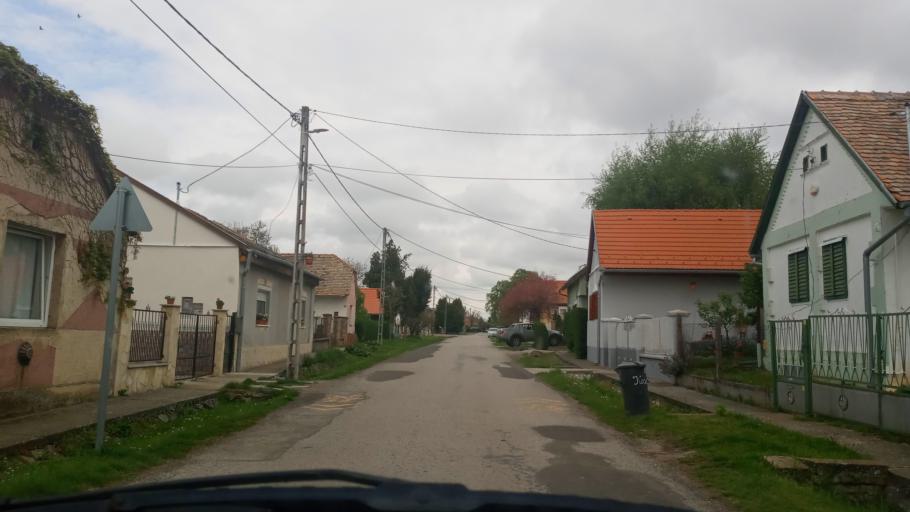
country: HU
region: Baranya
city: Kozarmisleny
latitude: 45.9979
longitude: 18.3757
